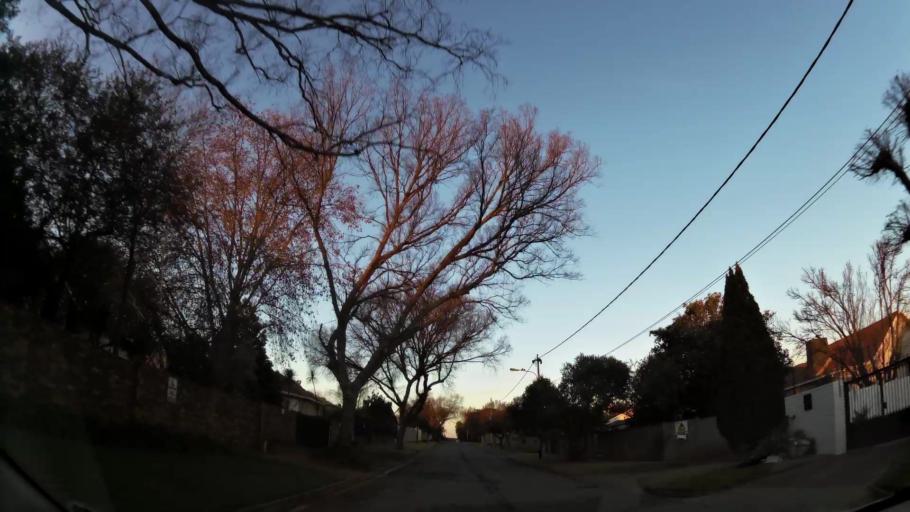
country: ZA
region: Gauteng
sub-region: City of Johannesburg Metropolitan Municipality
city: Roodepoort
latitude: -26.1573
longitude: 27.9110
